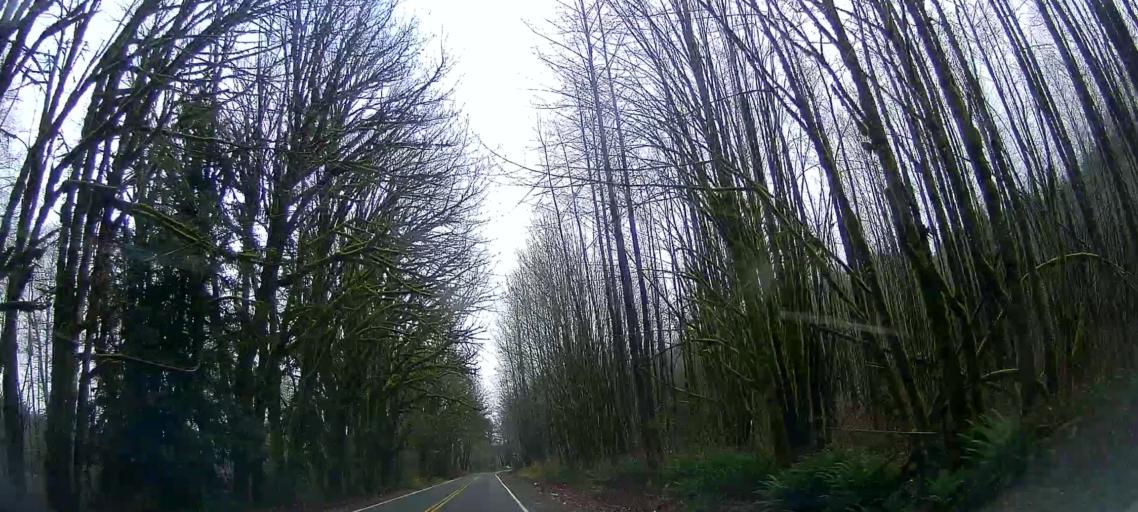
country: US
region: Washington
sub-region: Skagit County
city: Sedro-Woolley
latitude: 48.5115
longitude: -121.9076
